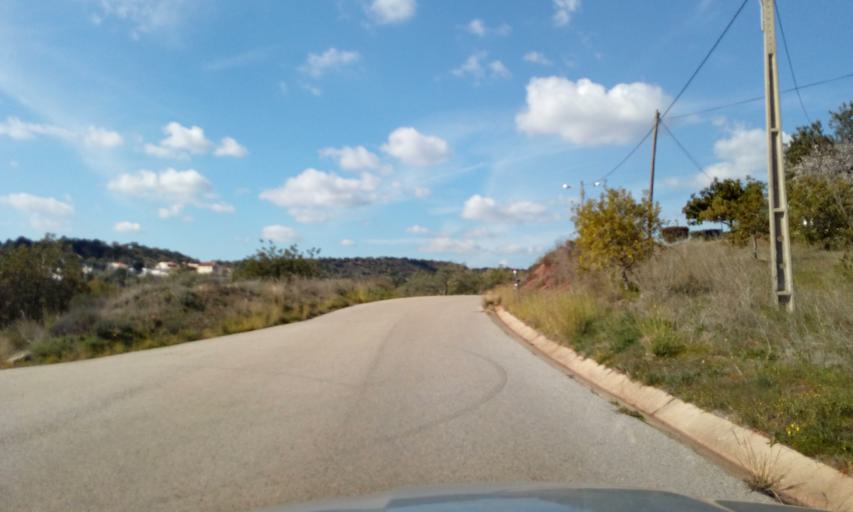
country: PT
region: Faro
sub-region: Loule
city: Loule
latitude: 37.2469
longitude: -8.0866
